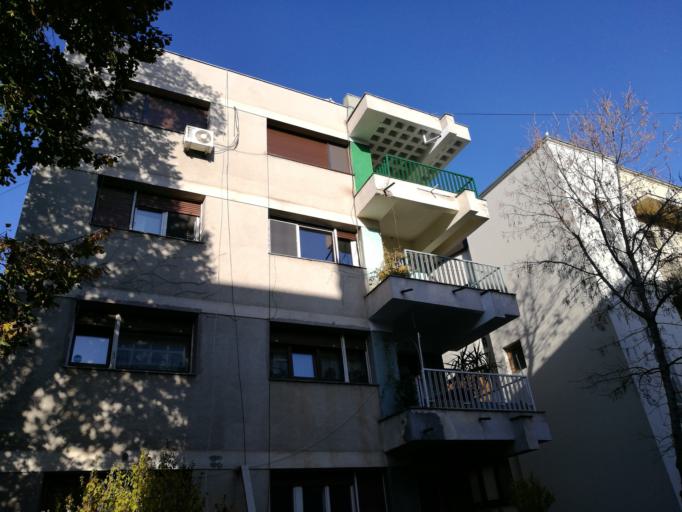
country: RO
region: Bucuresti
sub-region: Municipiul Bucuresti
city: Bucharest
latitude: 44.4639
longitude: 26.0949
